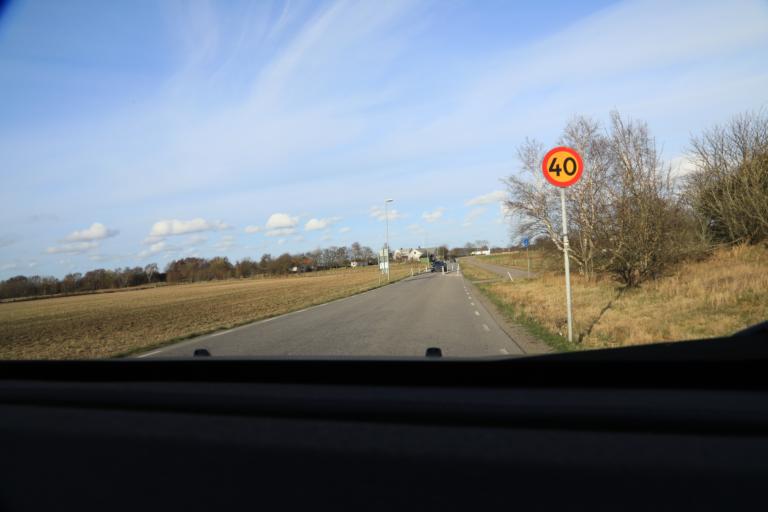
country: SE
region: Halland
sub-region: Varbergs Kommun
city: Varberg
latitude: 57.1198
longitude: 12.2166
